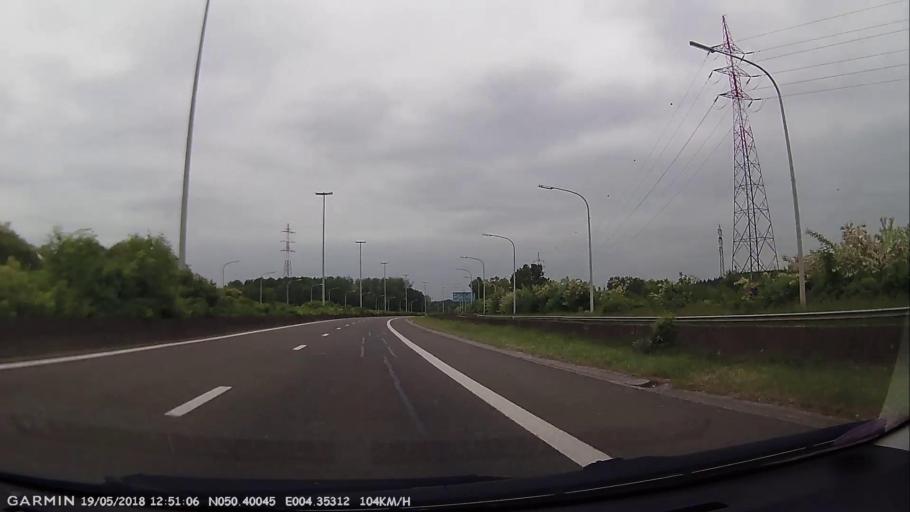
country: BE
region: Wallonia
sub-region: Province du Hainaut
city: Courcelles
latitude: 50.4008
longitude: 4.3524
